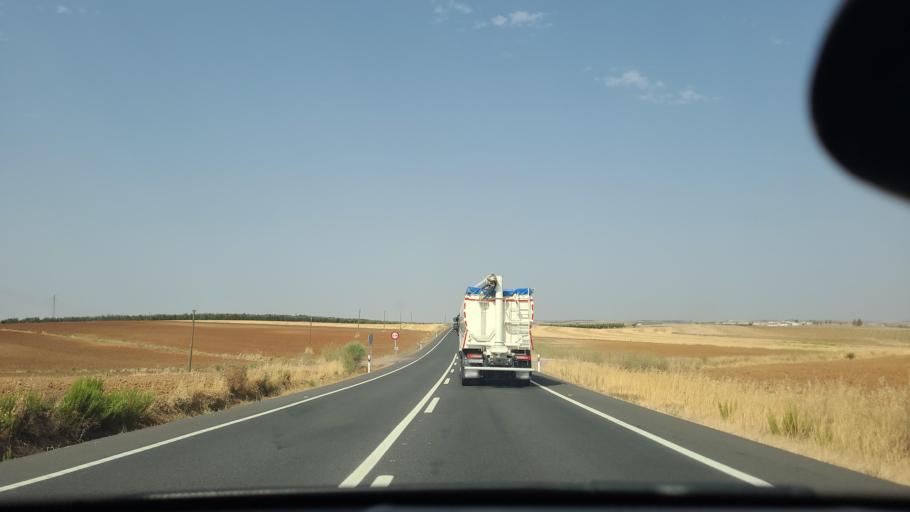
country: ES
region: Extremadura
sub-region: Provincia de Badajoz
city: Berlanga
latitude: 38.2664
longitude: -5.7773
